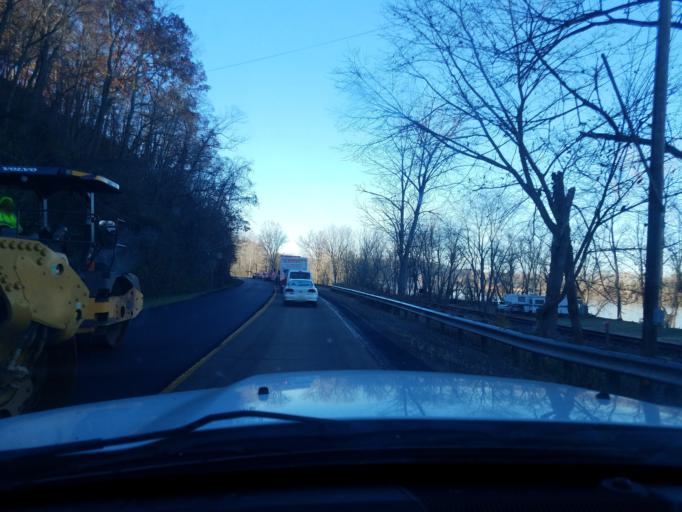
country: US
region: West Virginia
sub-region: Jackson County
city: Ravenswood
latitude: 38.8787
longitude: -81.8720
